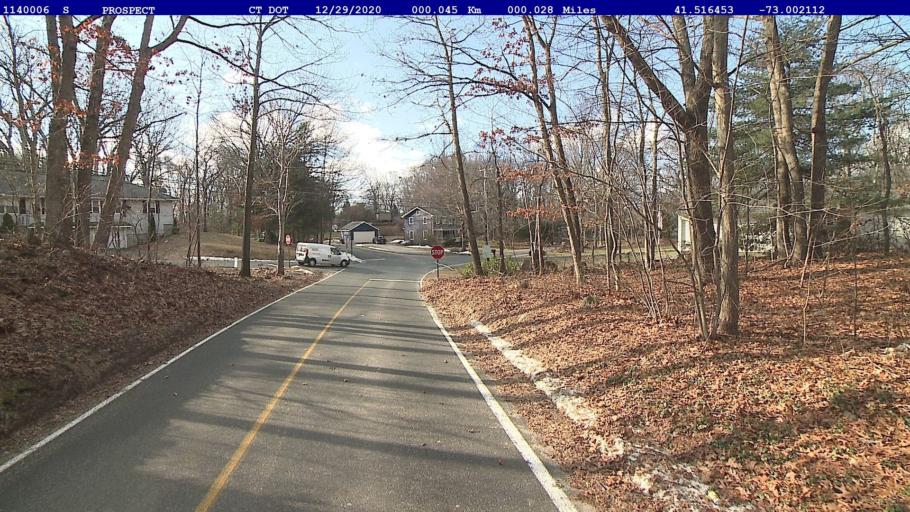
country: US
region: Connecticut
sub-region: New Haven County
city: Prospect
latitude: 41.5164
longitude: -73.0021
